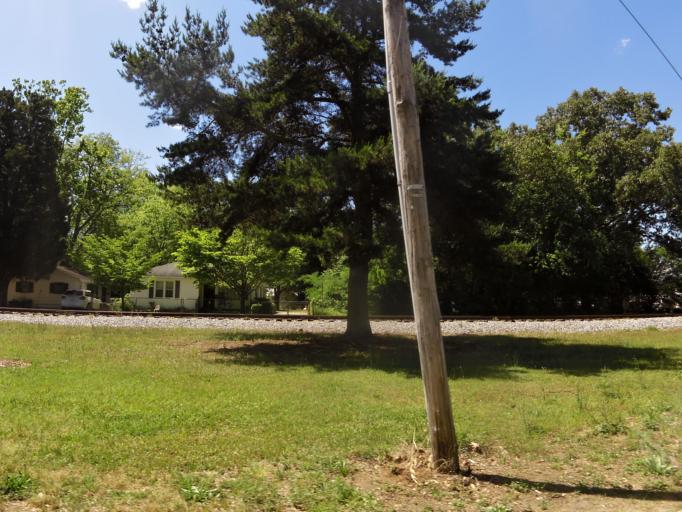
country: US
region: South Carolina
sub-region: Aiken County
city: Aiken
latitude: 33.5663
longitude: -81.7116
